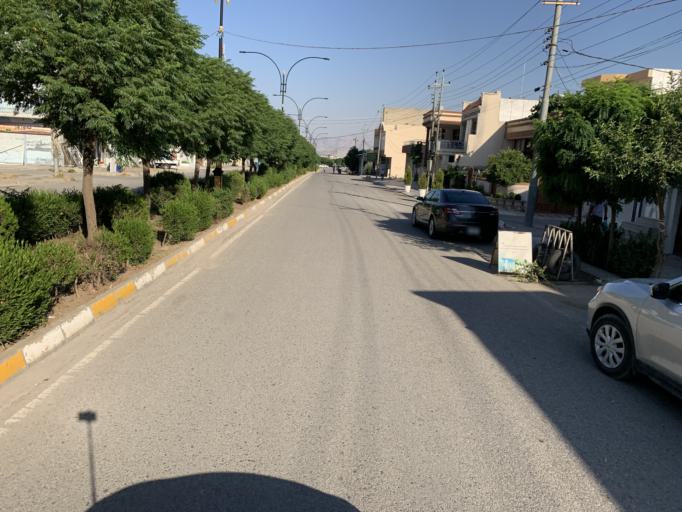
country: IQ
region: As Sulaymaniyah
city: Raniye
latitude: 36.2421
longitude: 44.8731
